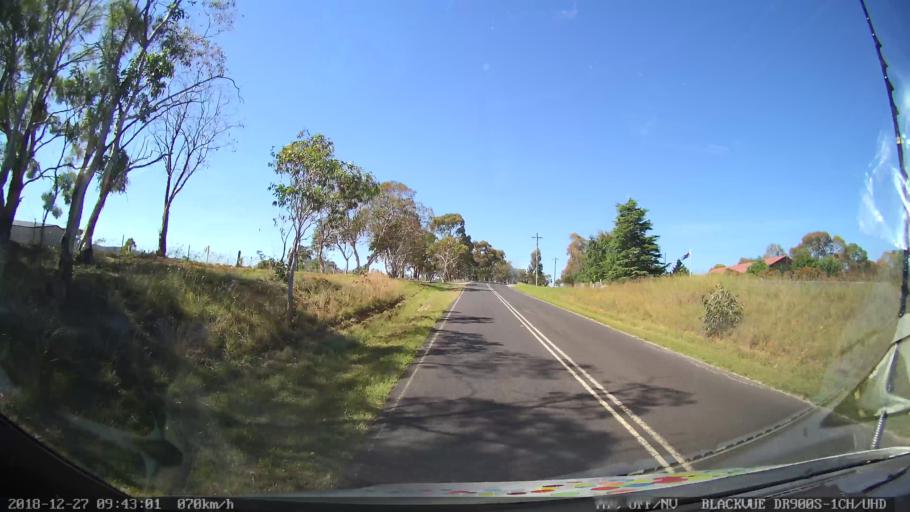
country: AU
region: New South Wales
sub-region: Lithgow
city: Portland
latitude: -33.3024
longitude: 150.0040
